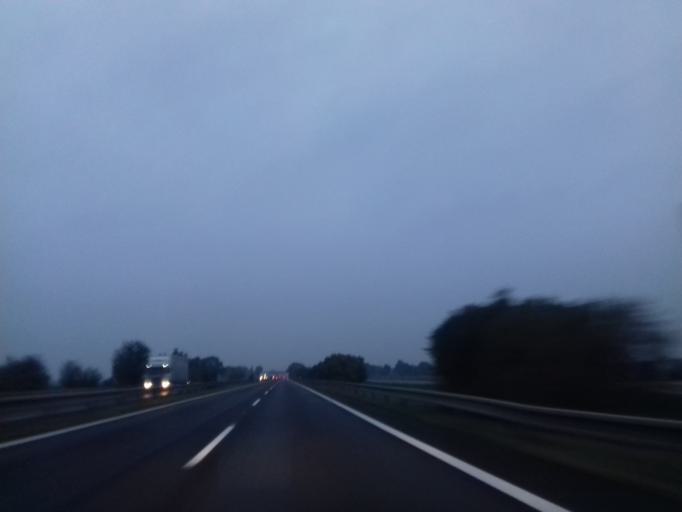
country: CZ
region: Olomoucky
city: Naklo
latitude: 49.6566
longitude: 17.1137
